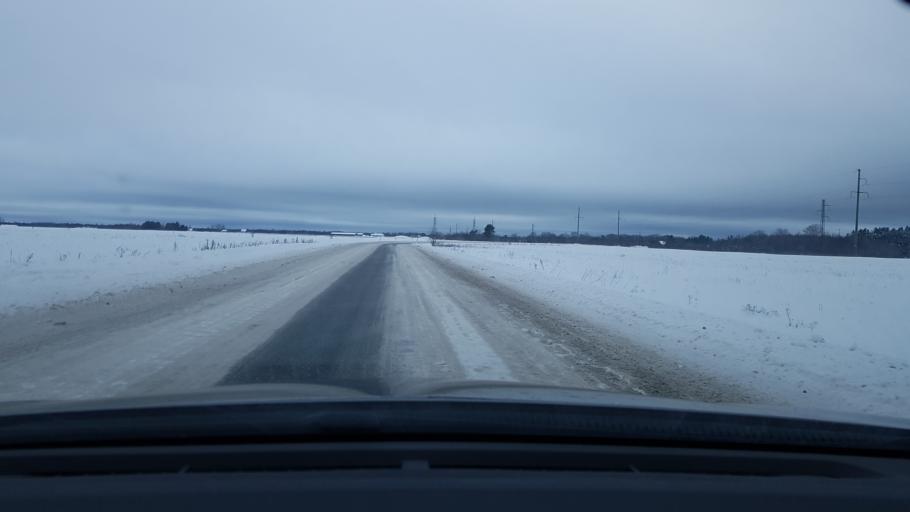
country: EE
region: Harju
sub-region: Harku vald
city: Tabasalu
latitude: 59.3917
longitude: 24.5534
